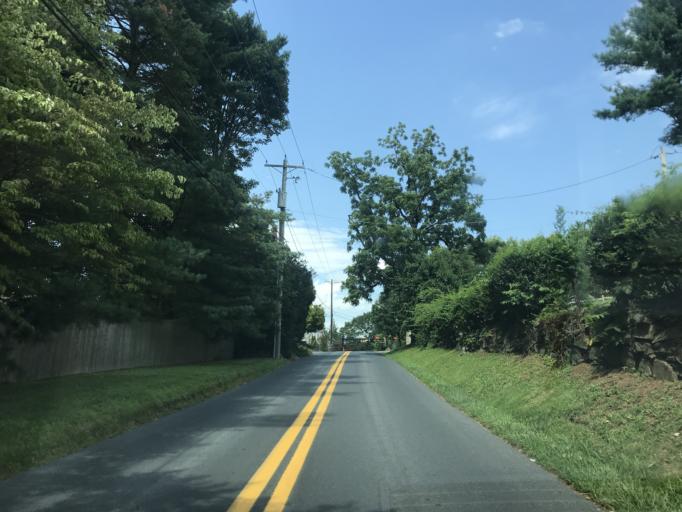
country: US
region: Delaware
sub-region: New Castle County
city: Greenville
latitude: 39.8207
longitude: -75.6177
